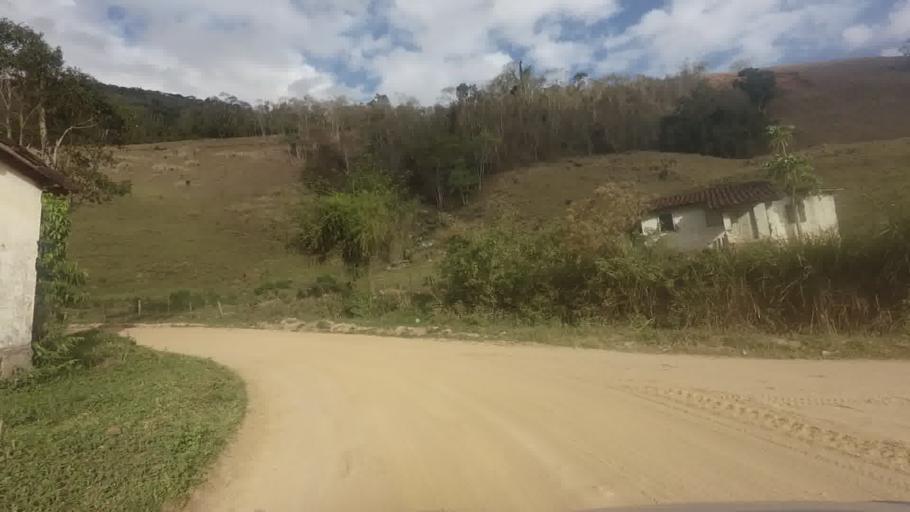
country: BR
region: Espirito Santo
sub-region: Mimoso Do Sul
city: Mimoso do Sul
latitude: -20.9696
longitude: -41.4516
